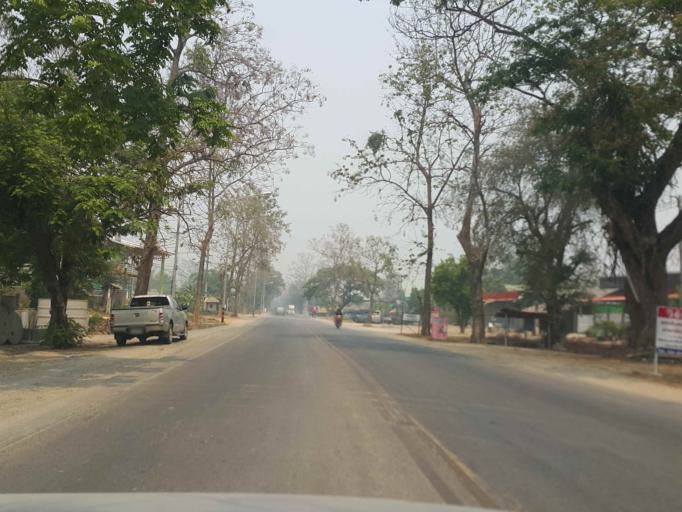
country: TH
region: Chiang Mai
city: Mae Taeng
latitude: 18.9927
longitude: 98.9782
